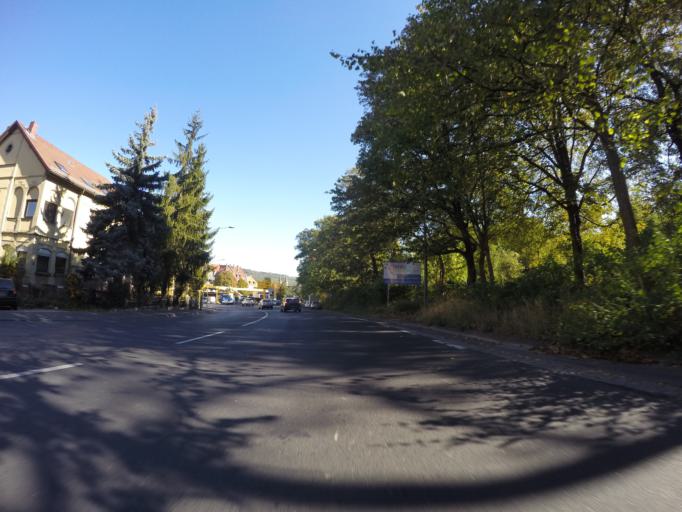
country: DE
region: Bavaria
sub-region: Regierungsbezirk Unterfranken
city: Hochberg
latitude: 49.7918
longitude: 9.9159
